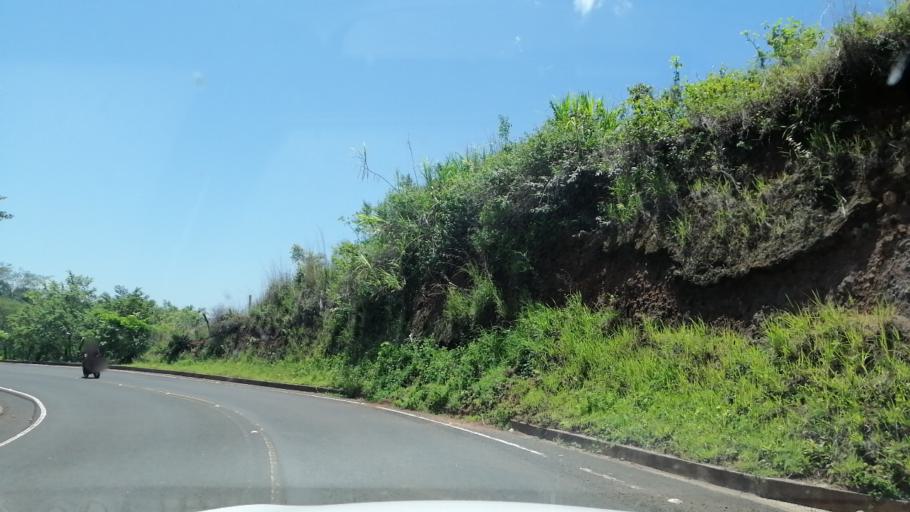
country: SV
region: San Miguel
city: Ciudad Barrios
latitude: 13.7904
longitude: -88.2882
